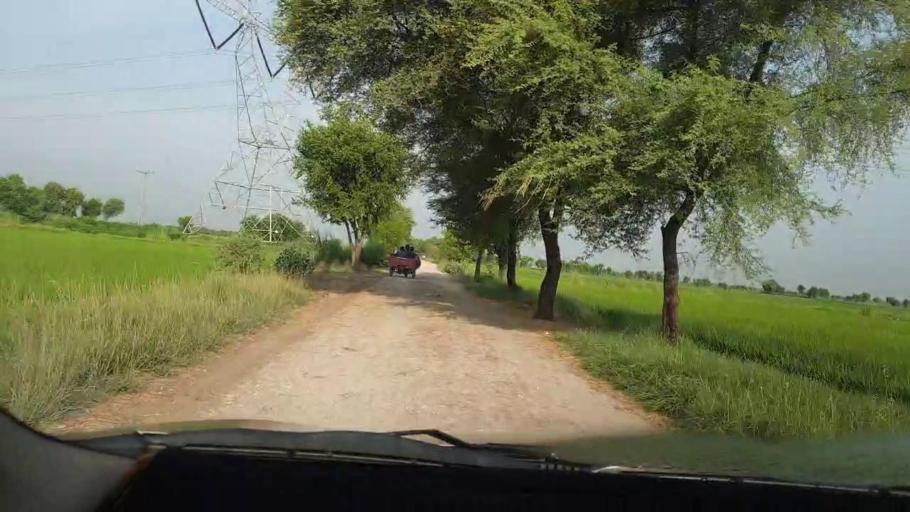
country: PK
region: Sindh
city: Goth Garelo
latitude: 27.4822
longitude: 68.0807
